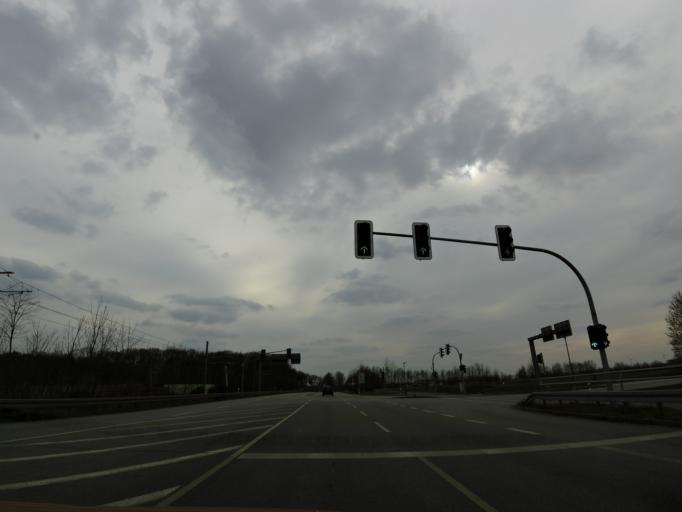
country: DE
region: Brandenburg
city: Frankfurt (Oder)
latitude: 52.3077
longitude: 14.4859
